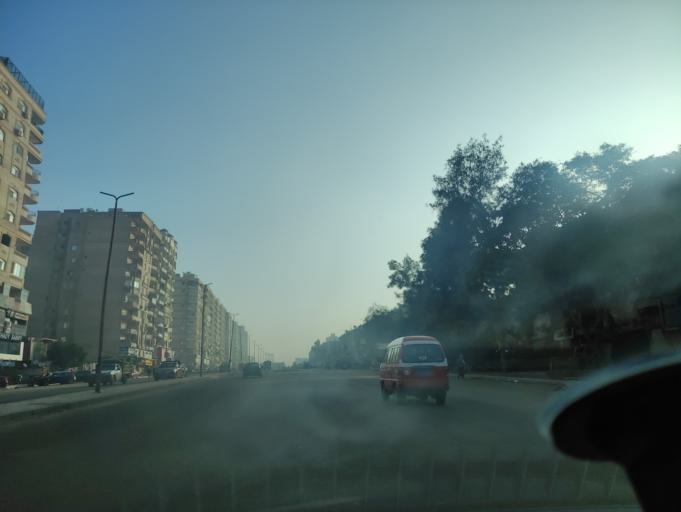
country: EG
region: Muhafazat al Qahirah
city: Cairo
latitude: 30.0486
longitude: 31.3719
